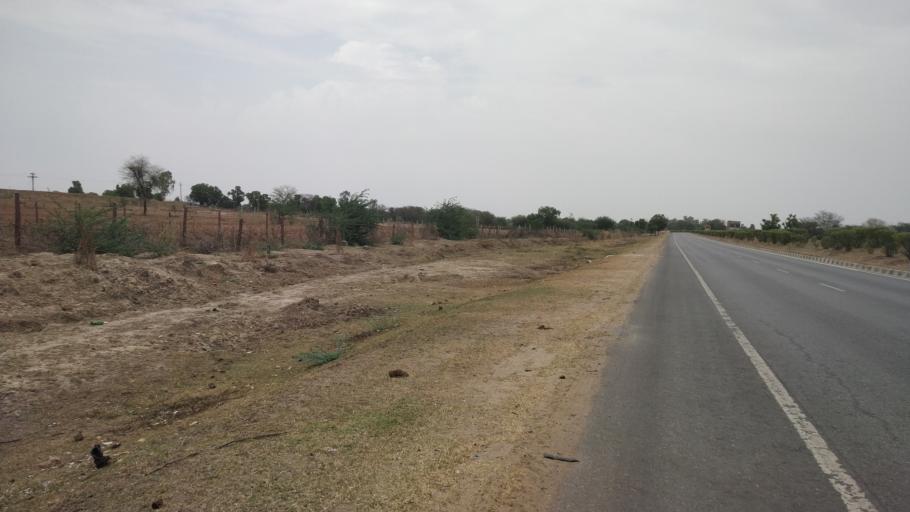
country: IN
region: Rajasthan
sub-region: Tonk
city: Todaraisingh
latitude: 25.9609
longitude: 75.6458
